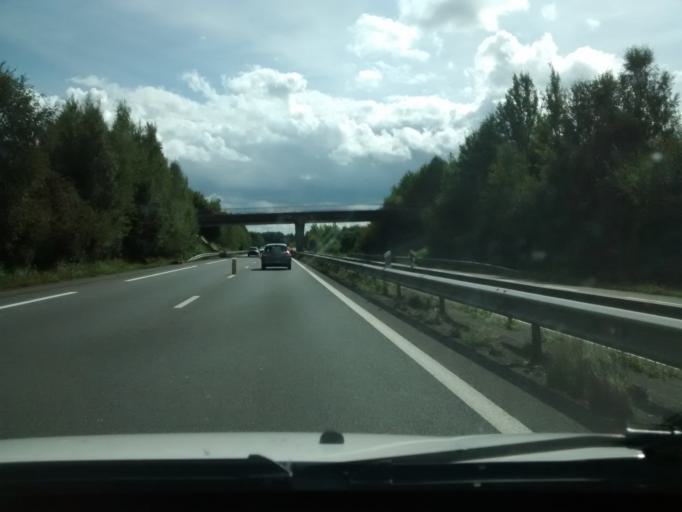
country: FR
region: Brittany
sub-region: Departement d'Ille-et-Vilaine
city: Saint-Domineuc
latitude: 48.3758
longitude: -1.8919
